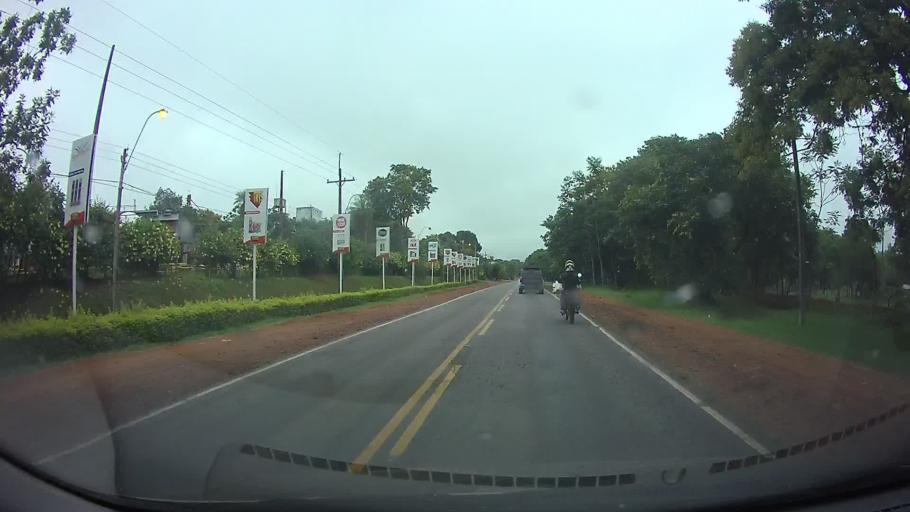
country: PY
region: Central
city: Itaugua
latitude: -25.4065
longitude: -57.3592
